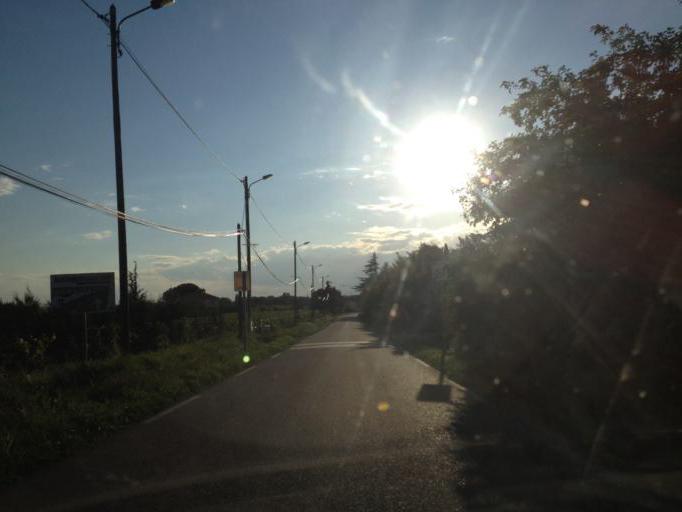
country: FR
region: Provence-Alpes-Cote d'Azur
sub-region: Departement du Vaucluse
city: Sablet
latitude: 44.1935
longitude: 4.9998
